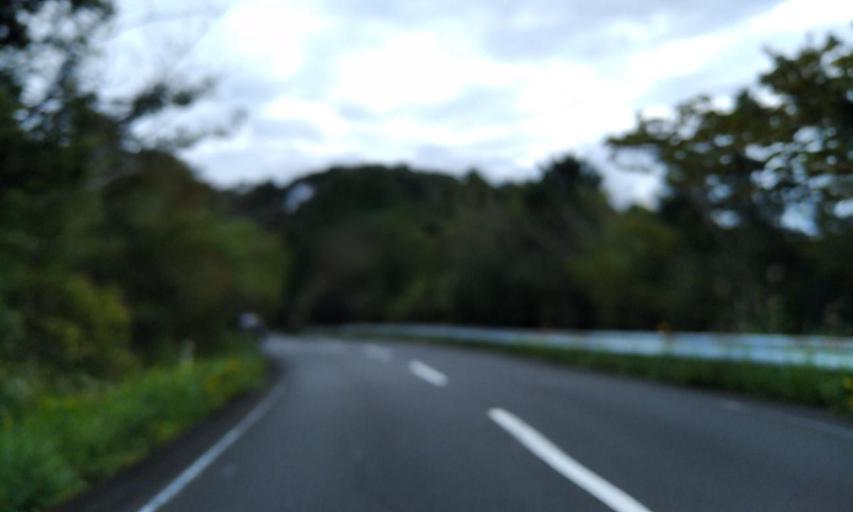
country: JP
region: Wakayama
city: Shingu
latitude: 33.4698
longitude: 135.8209
